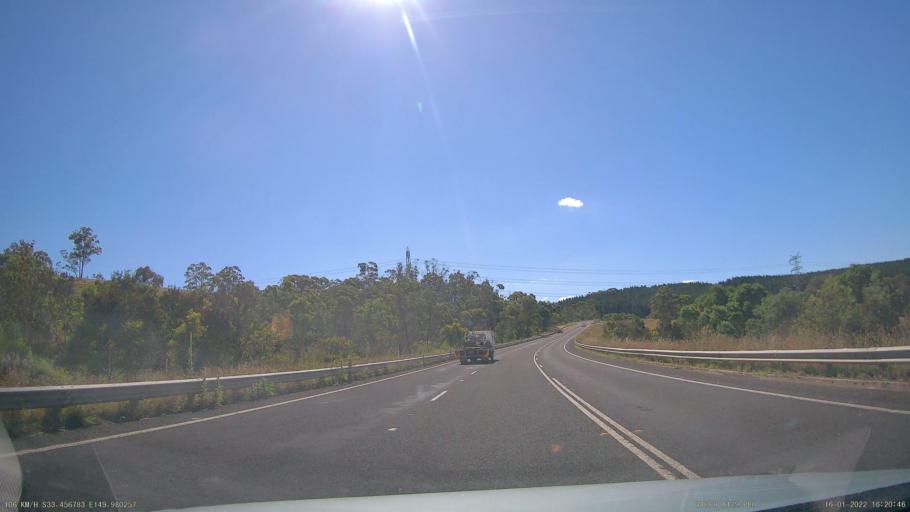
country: AU
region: New South Wales
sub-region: Lithgow
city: Portland
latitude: -33.4571
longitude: 149.9796
